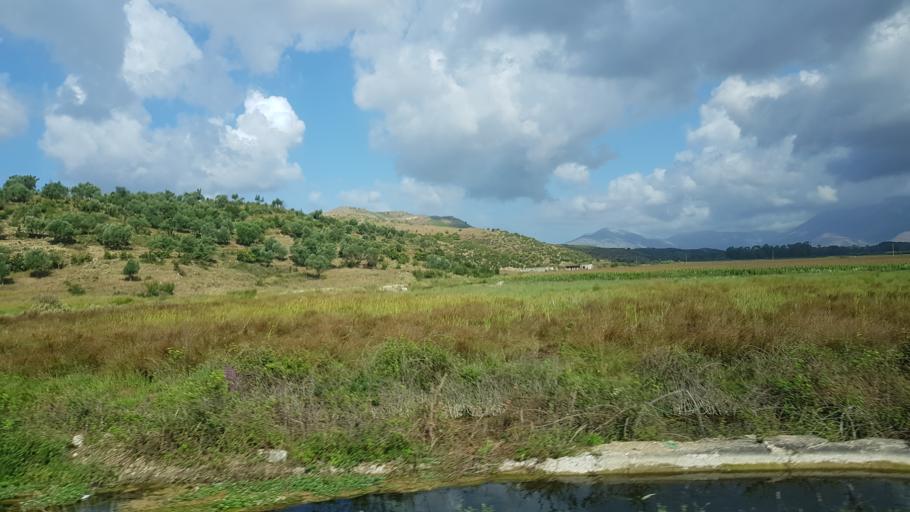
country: AL
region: Vlore
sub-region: Rrethi i Delvines
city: Mesopotam
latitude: 39.9052
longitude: 20.0853
